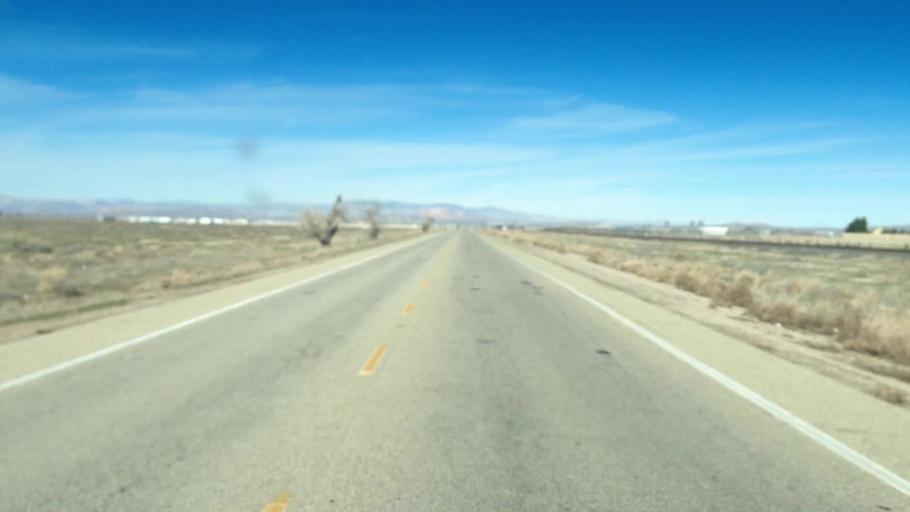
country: US
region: California
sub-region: Los Angeles County
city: Lancaster
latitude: 34.7273
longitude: -118.1412
